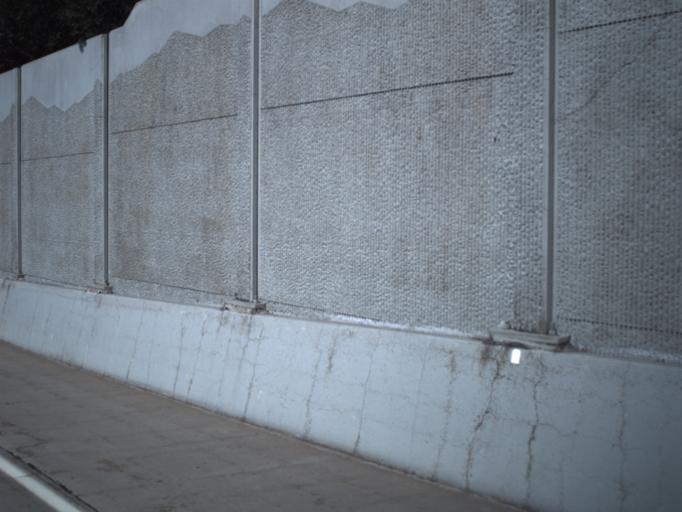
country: US
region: Utah
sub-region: Salt Lake County
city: Midvale
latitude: 40.6374
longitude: -111.9068
